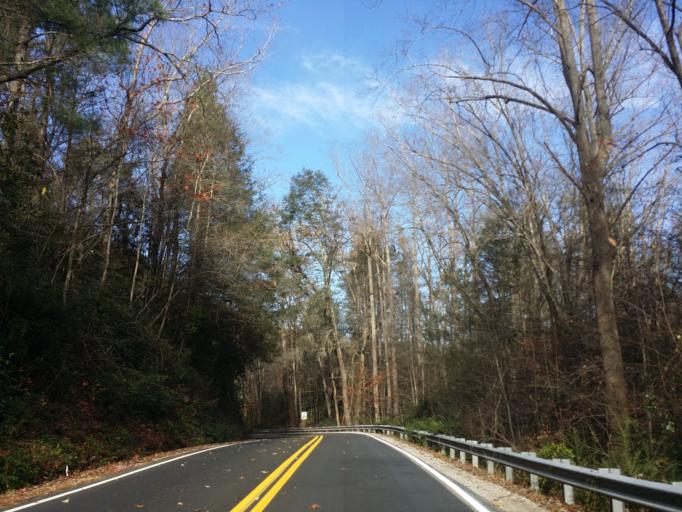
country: US
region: North Carolina
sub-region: McDowell County
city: Marion
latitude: 35.7205
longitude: -82.0778
